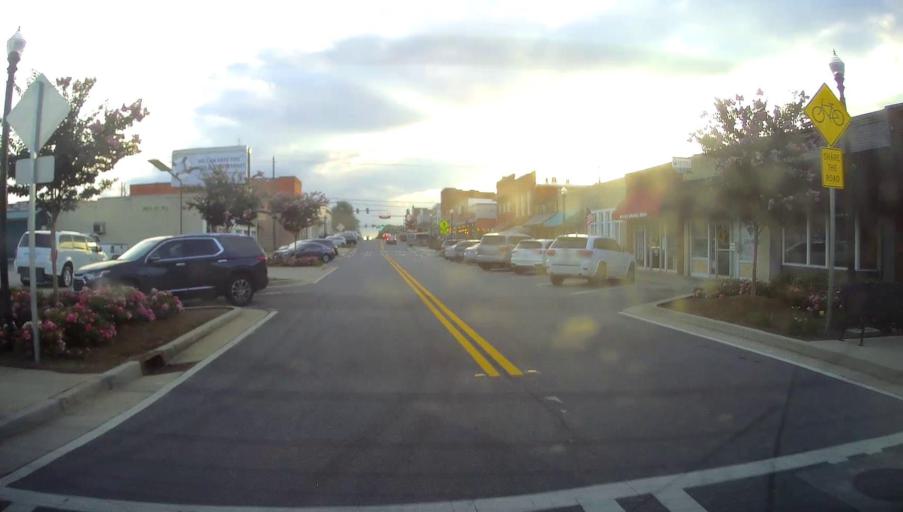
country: US
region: Georgia
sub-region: Monroe County
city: Forsyth
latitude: 33.0349
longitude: -83.9371
